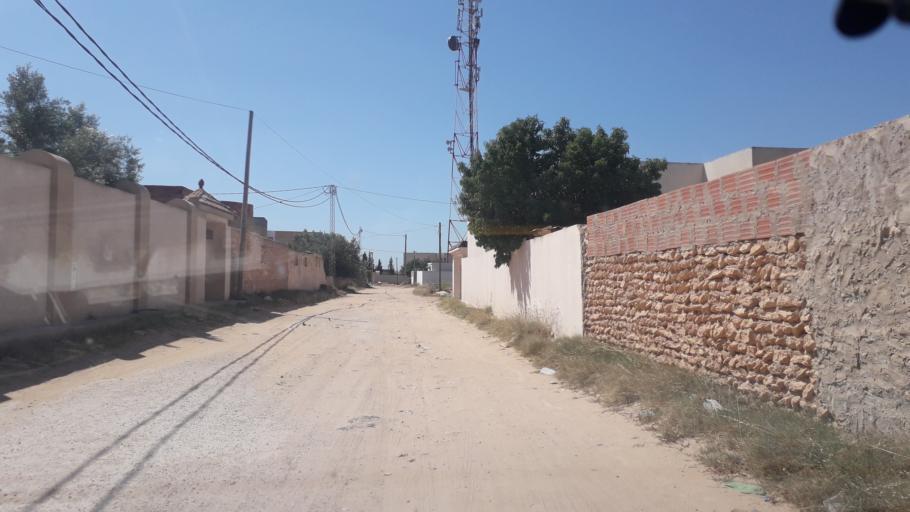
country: TN
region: Safaqis
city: Al Qarmadah
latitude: 34.8282
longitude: 10.7664
